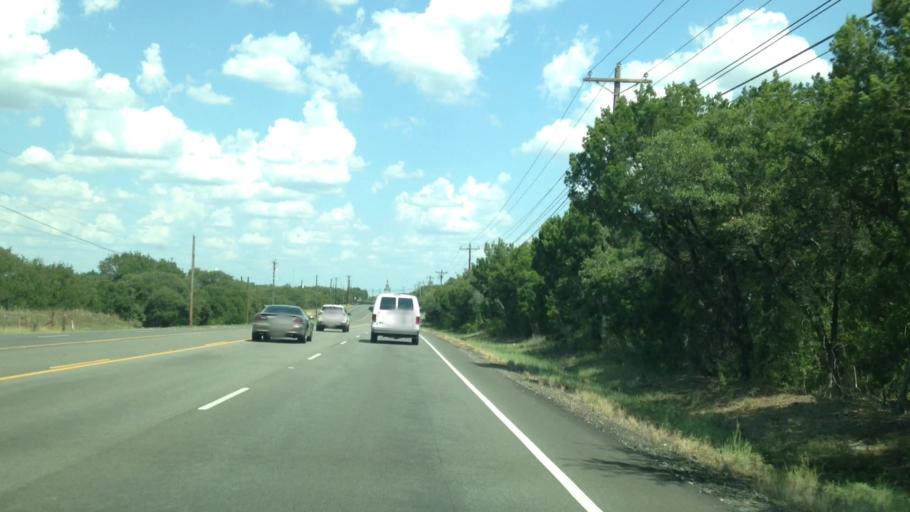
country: US
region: Texas
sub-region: Williamson County
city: Georgetown
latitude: 30.6335
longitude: -97.7185
